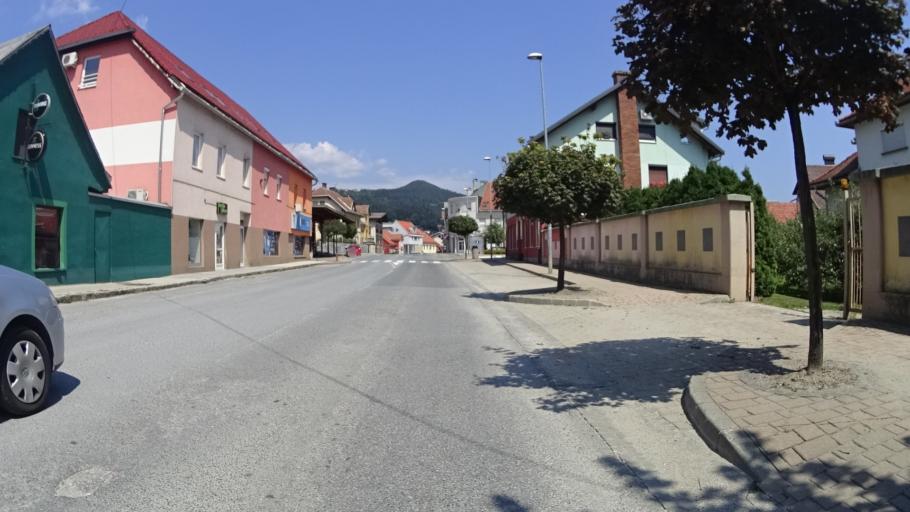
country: SI
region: Prevalje
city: Prevalje
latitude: 46.5452
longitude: 14.9151
